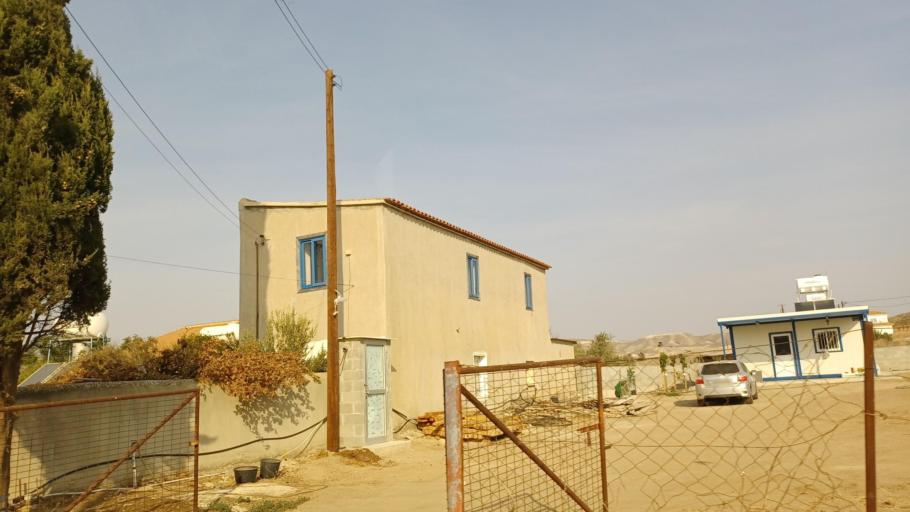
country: CY
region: Larnaka
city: Troulloi
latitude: 35.0337
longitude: 33.6117
